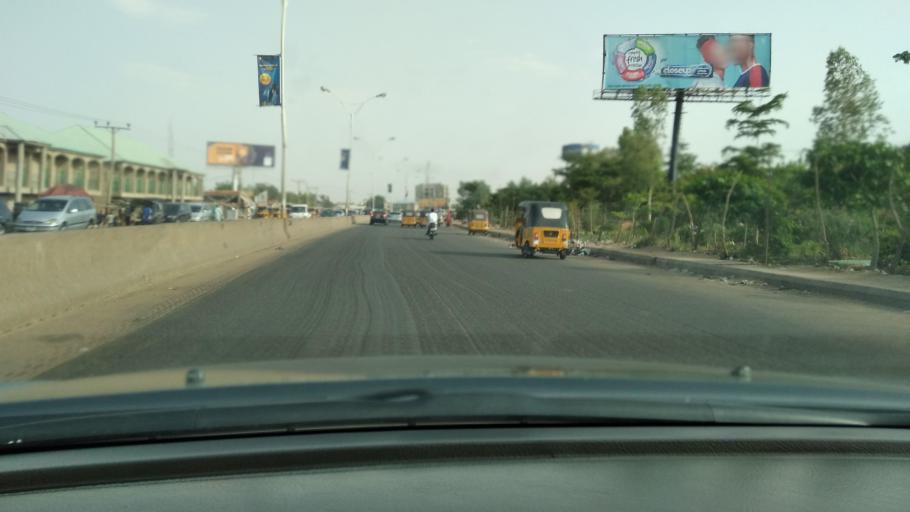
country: NG
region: Kano
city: Kano
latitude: 11.9495
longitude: 8.5655
